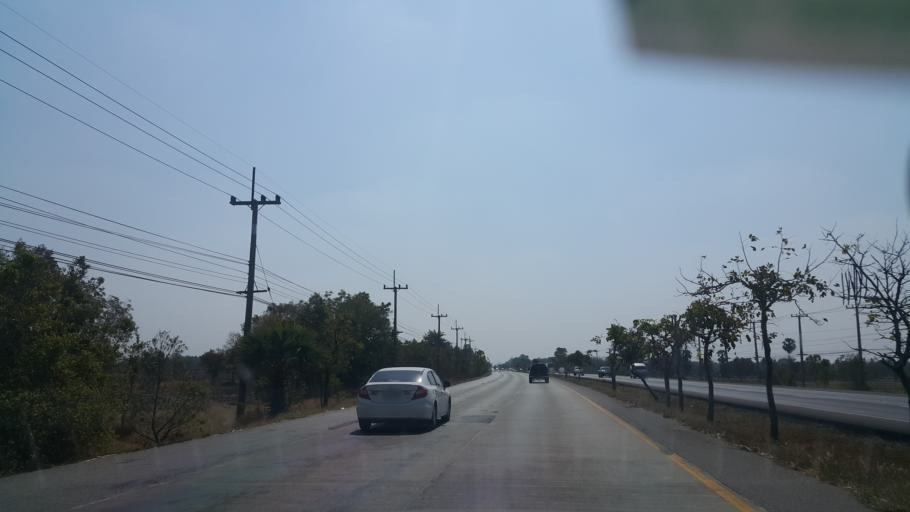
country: TH
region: Nakhon Ratchasima
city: Non Daeng
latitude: 15.4694
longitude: 102.5089
